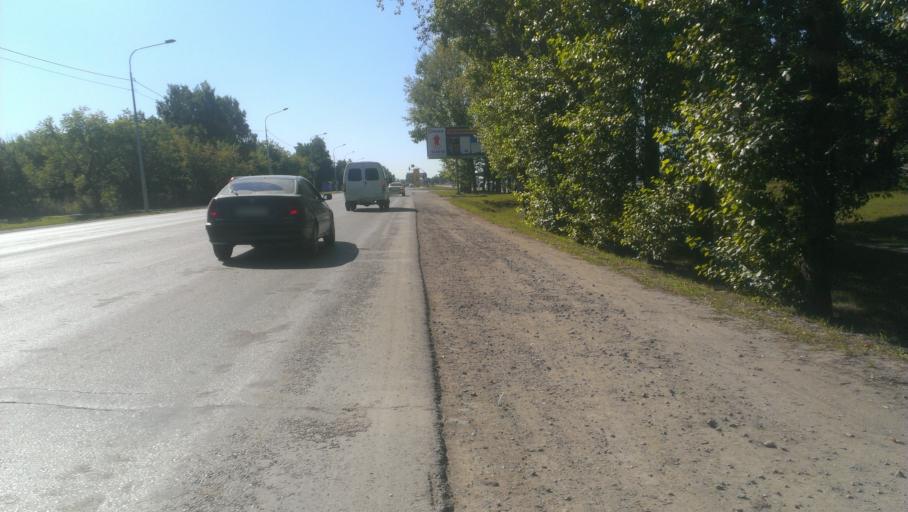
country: RU
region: Altai Krai
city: Novosilikatnyy
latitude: 53.3474
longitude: 83.6414
